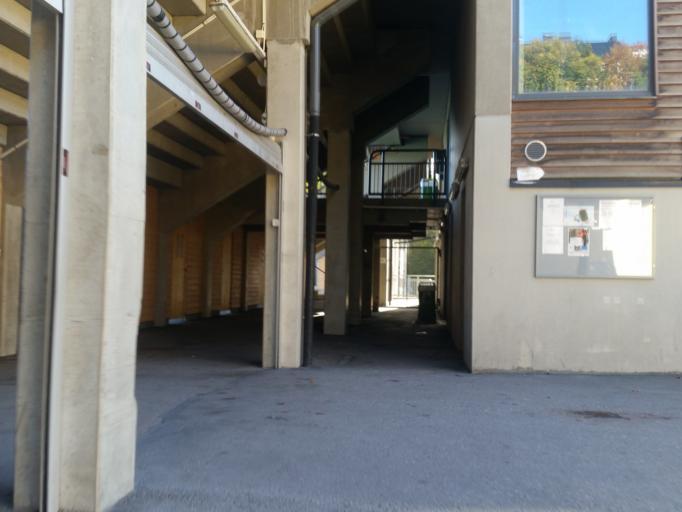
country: SE
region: Stockholm
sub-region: Stockholms Kommun
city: Arsta
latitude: 59.3158
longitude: 18.0492
